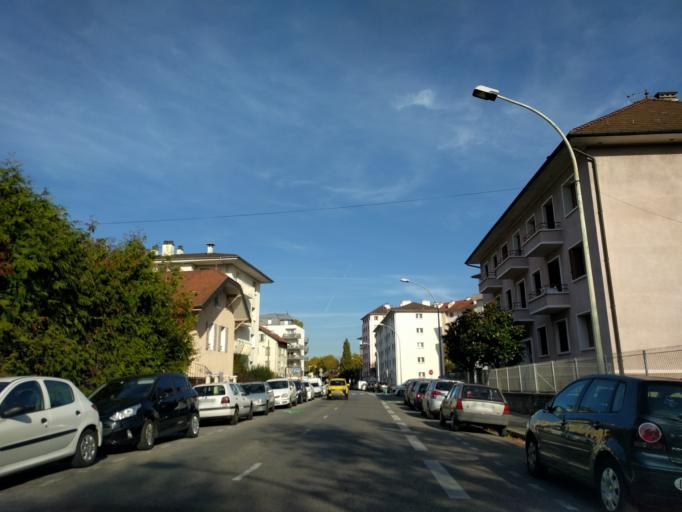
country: FR
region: Rhone-Alpes
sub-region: Departement de la Haute-Savoie
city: Annecy
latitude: 45.9130
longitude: 6.1220
